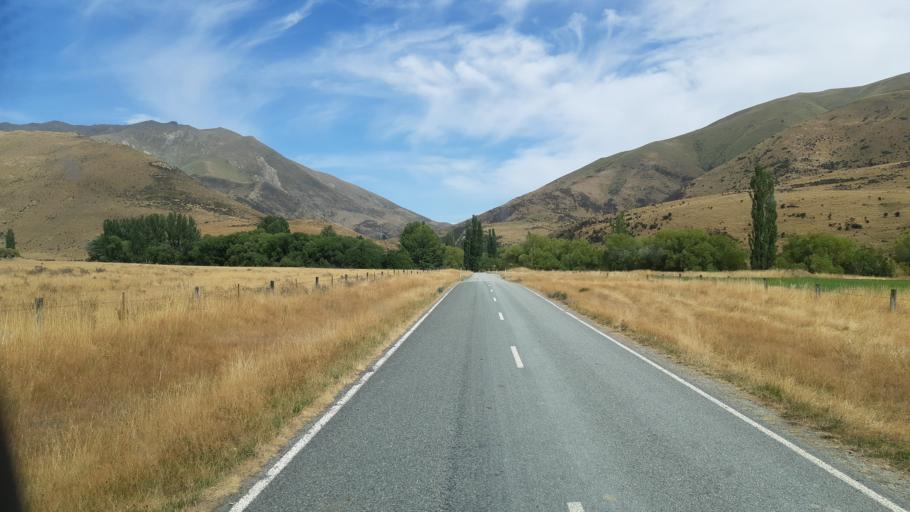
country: NZ
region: Canterbury
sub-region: Timaru District
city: Pleasant Point
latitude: -44.1881
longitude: 170.6629
